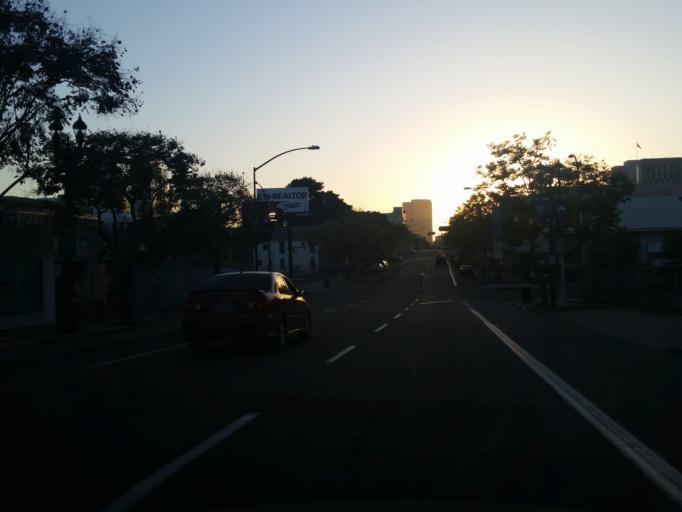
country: US
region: California
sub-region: San Diego County
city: San Diego
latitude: 32.7138
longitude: -117.1497
